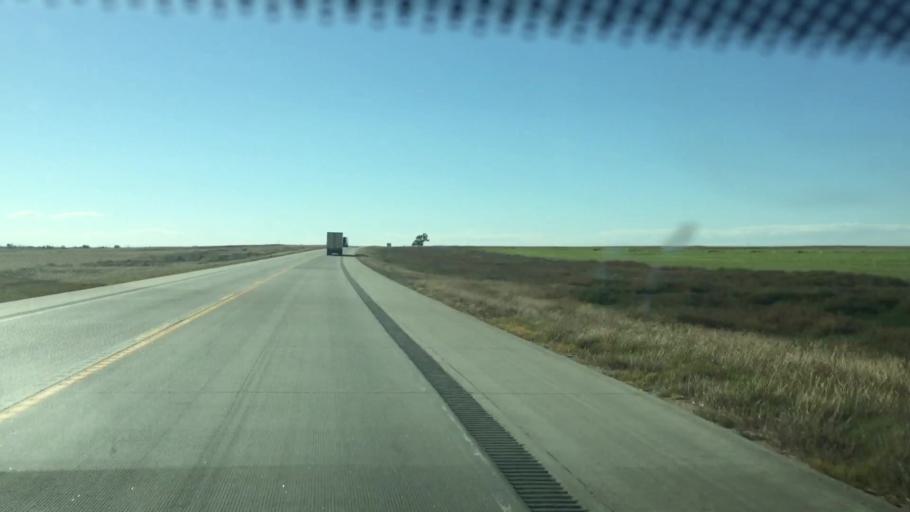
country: US
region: Colorado
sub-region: Kiowa County
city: Eads
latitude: 38.7638
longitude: -102.8192
